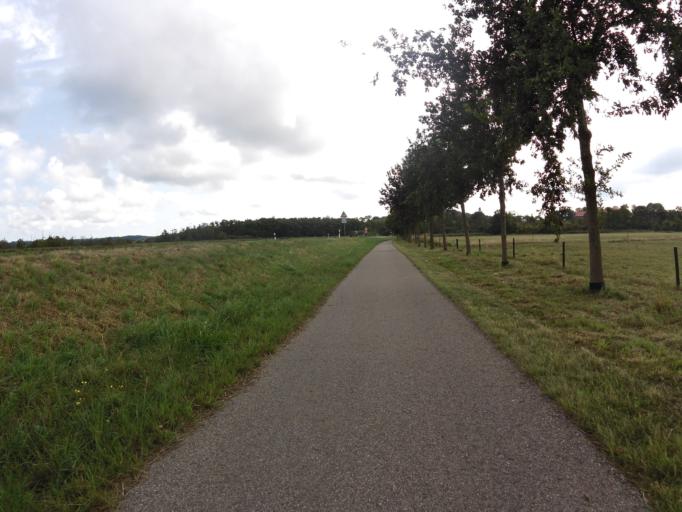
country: DE
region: Mecklenburg-Vorpommern
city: Seebad Bansin
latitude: 53.9733
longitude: 14.0726
